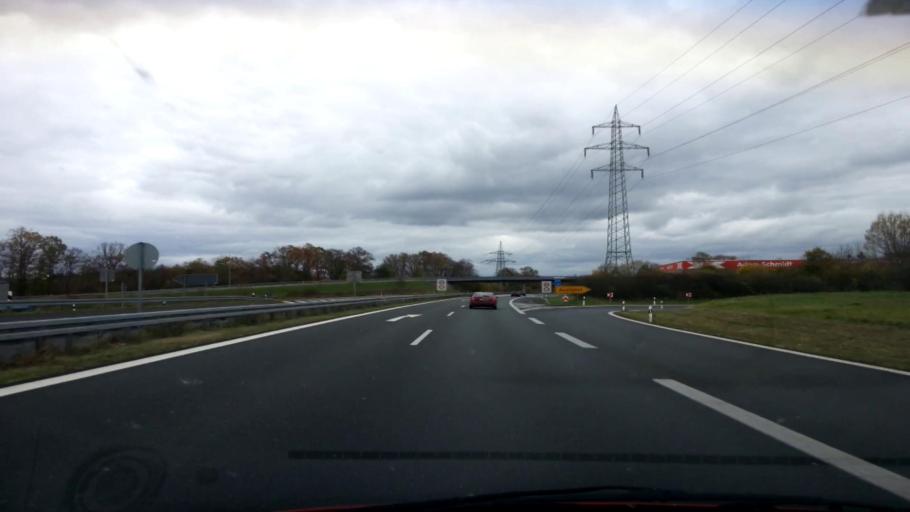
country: DE
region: Bavaria
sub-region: Upper Franconia
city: Lichtenfels
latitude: 50.1491
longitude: 11.0842
